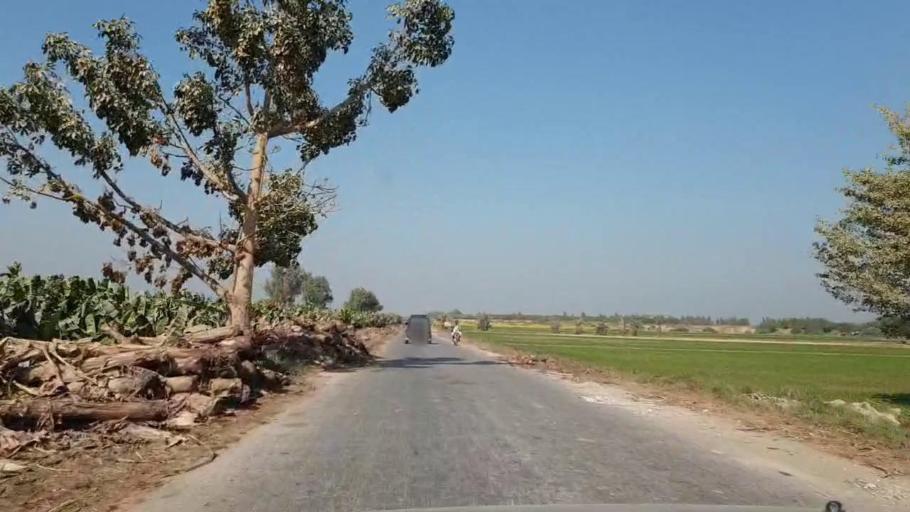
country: PK
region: Sindh
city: Tando Adam
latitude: 25.6463
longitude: 68.5922
